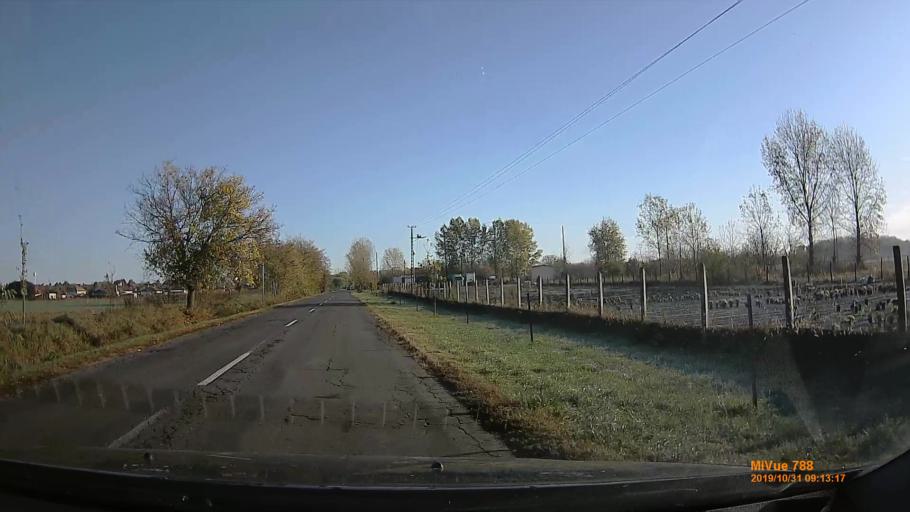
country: HU
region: Pest
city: Peteri
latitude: 47.3809
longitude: 19.4046
